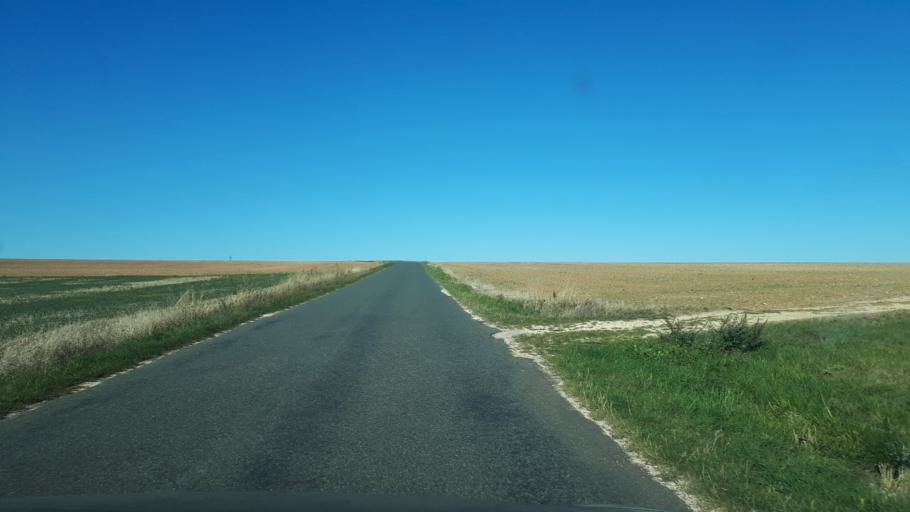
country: FR
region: Centre
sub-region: Departement du Cher
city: Baugy
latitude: 47.2144
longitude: 2.7482
